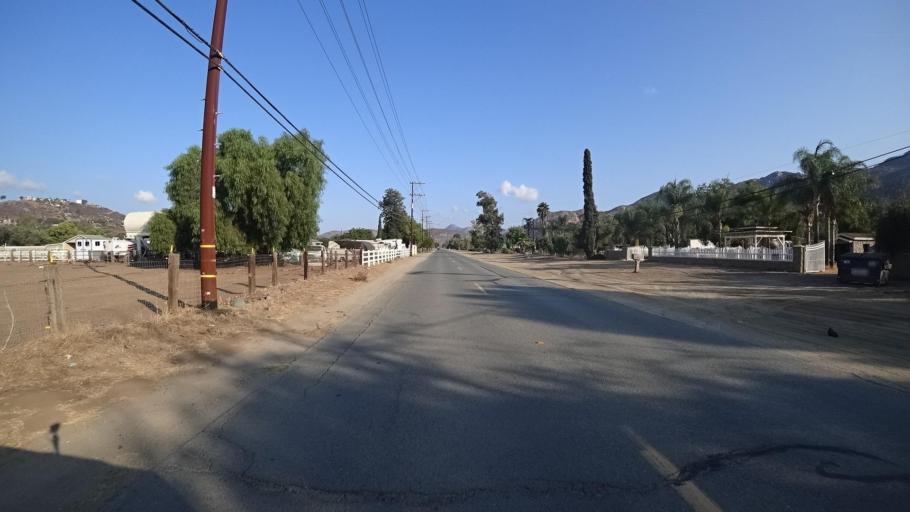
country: US
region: California
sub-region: San Diego County
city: Eucalyptus Hills
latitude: 32.8867
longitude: -116.9252
